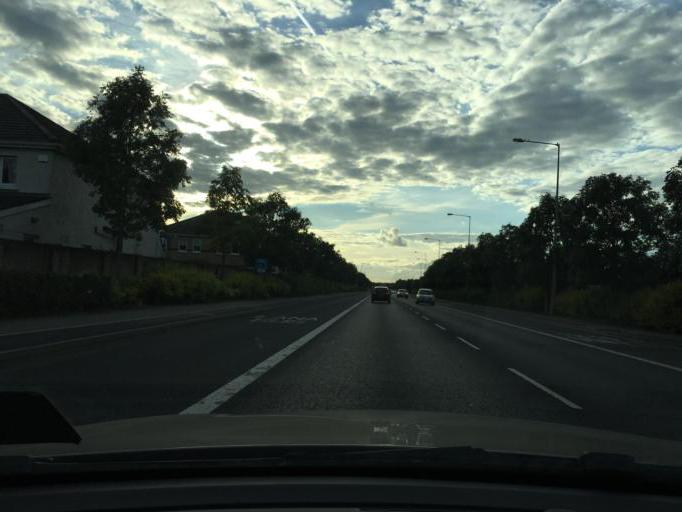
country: IE
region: Leinster
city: Hartstown
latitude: 53.3862
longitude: -6.4057
